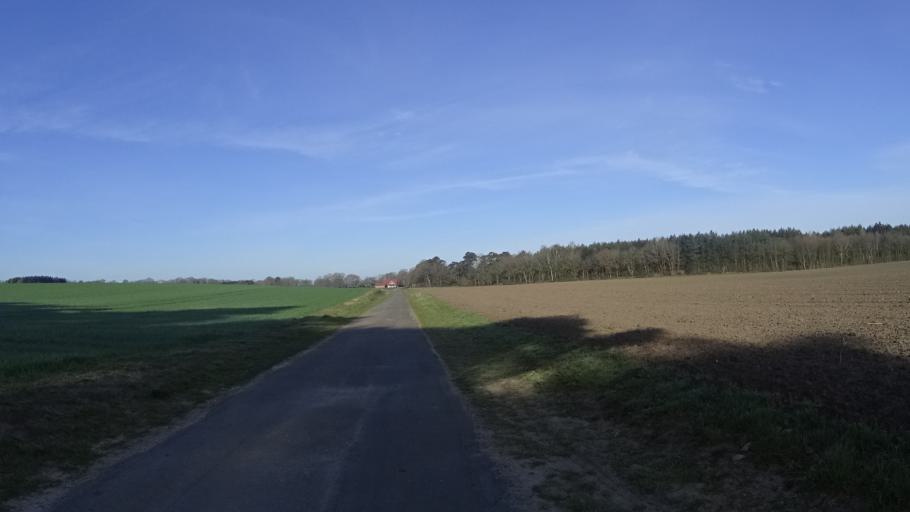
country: DE
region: Lower Saxony
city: Haren
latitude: 52.8133
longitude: 7.2674
